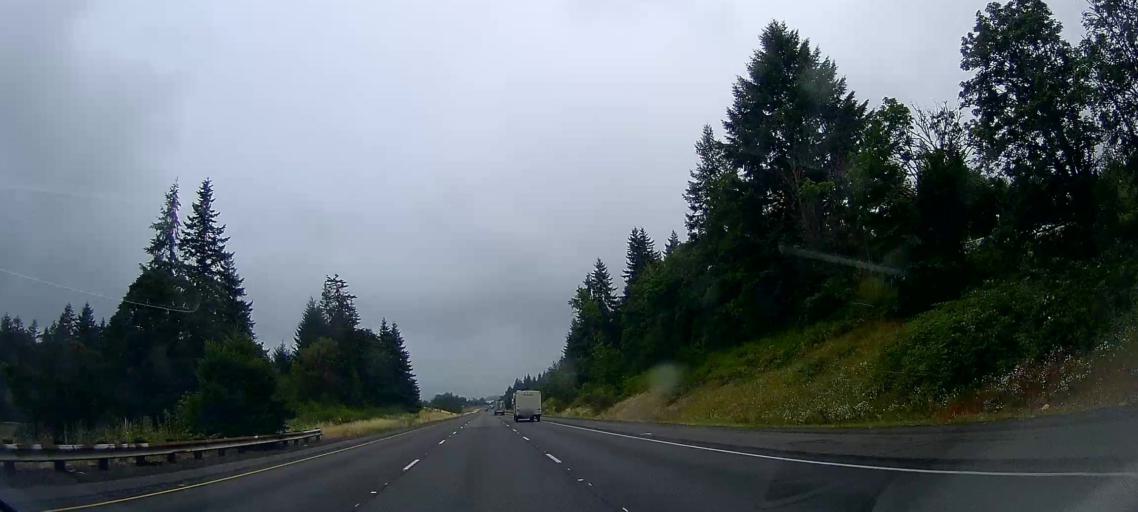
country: US
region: Washington
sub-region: Cowlitz County
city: Kalama
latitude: 45.9937
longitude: -122.8367
